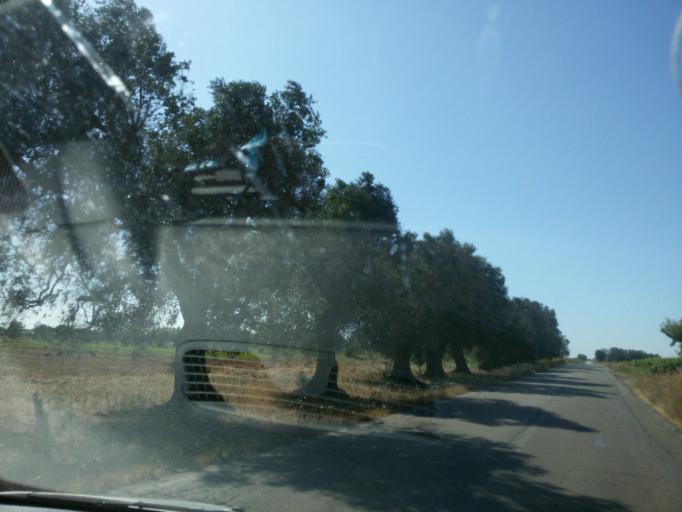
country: IT
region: Apulia
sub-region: Provincia di Brindisi
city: San Donaci
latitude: 40.4792
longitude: 17.8910
